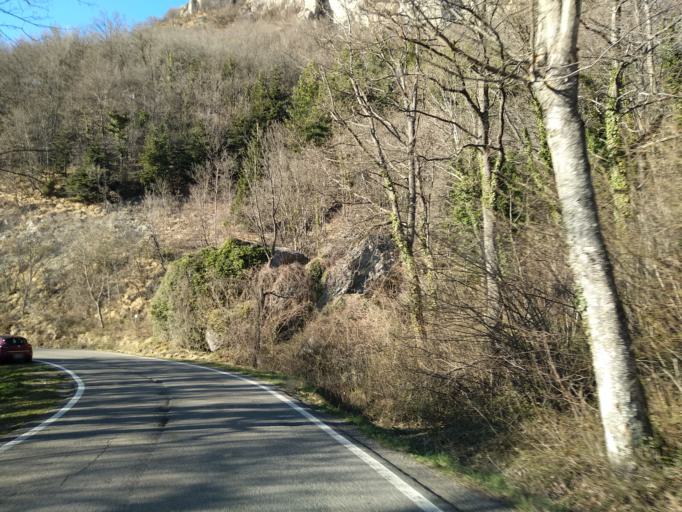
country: IT
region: Emilia-Romagna
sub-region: Provincia di Reggio Emilia
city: Castelnovo ne'Monti
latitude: 44.4175
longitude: 10.4101
